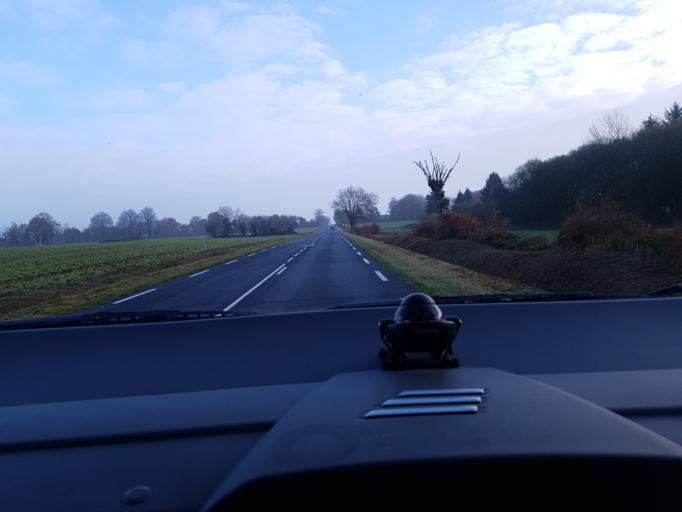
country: FR
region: Lower Normandy
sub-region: Departement de l'Orne
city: Magny-le-Desert
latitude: 48.6065
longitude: -0.3237
